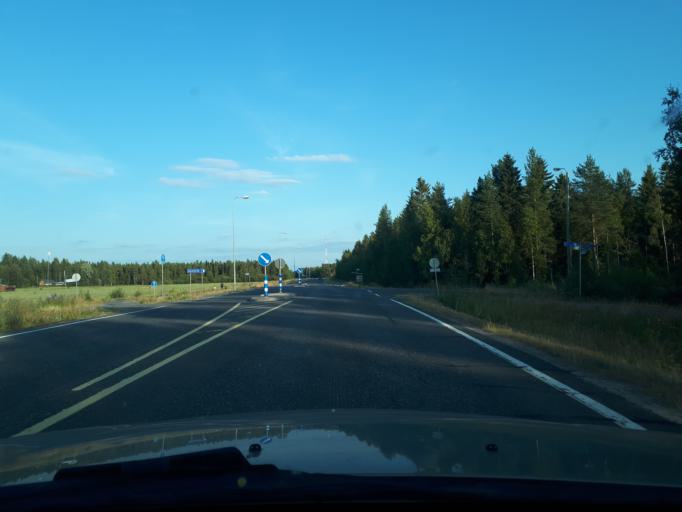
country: FI
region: Northern Ostrobothnia
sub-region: Oulu
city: Oulunsalo
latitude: 64.9792
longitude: 25.2760
